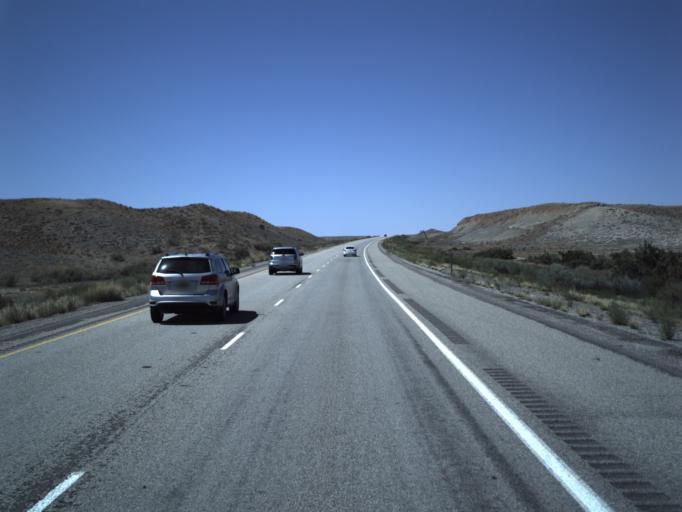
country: US
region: Utah
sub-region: Grand County
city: Moab
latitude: 38.9764
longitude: -109.3540
